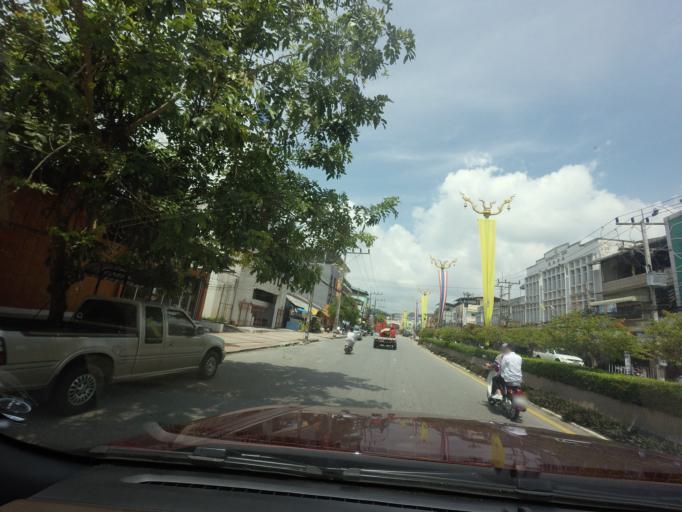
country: TH
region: Yala
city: Betong
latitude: 5.7761
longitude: 101.0730
